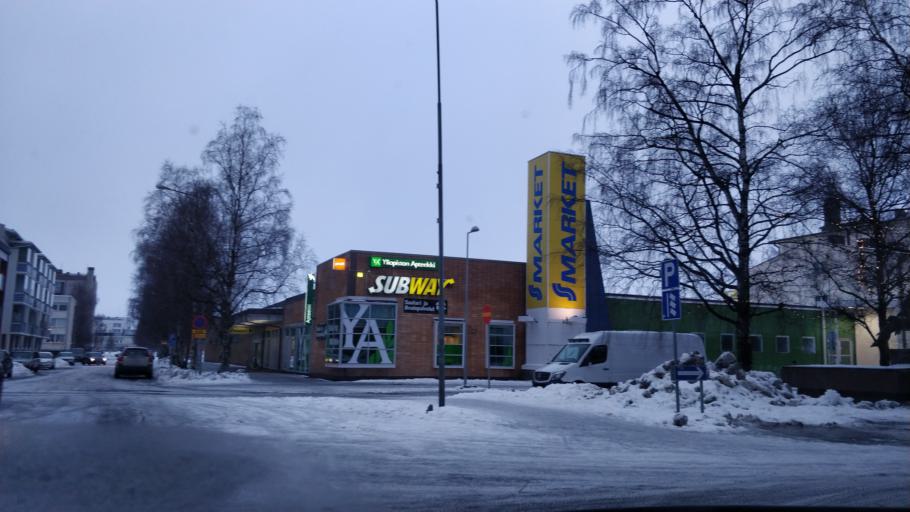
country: FI
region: Lapland
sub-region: Kemi-Tornio
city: Kemi
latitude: 65.7373
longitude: 24.5628
